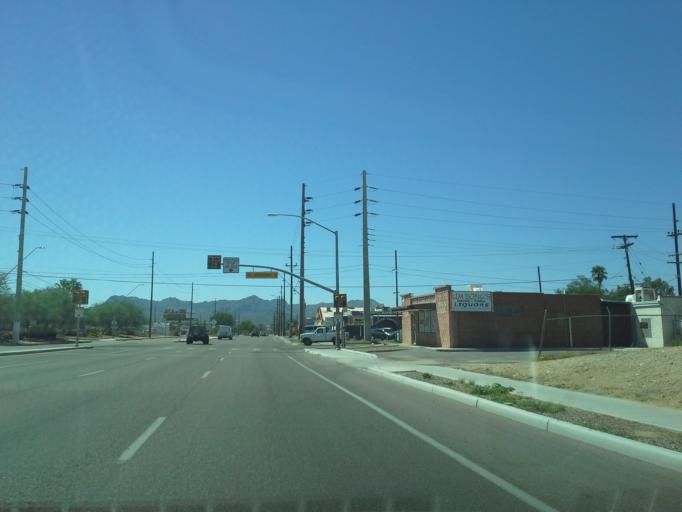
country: US
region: Arizona
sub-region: Pima County
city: Flowing Wells
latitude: 32.2503
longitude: -110.9816
